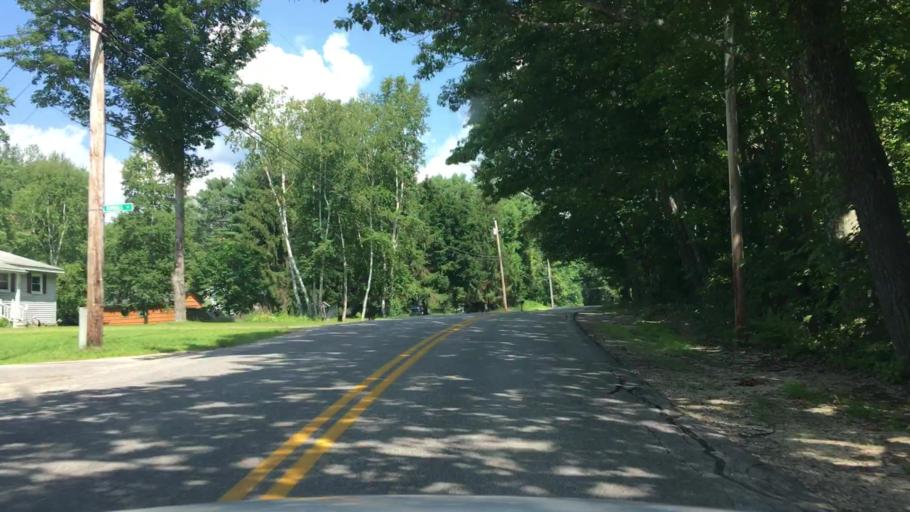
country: US
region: Maine
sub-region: Cumberland County
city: Raymond
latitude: 43.9446
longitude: -70.5258
